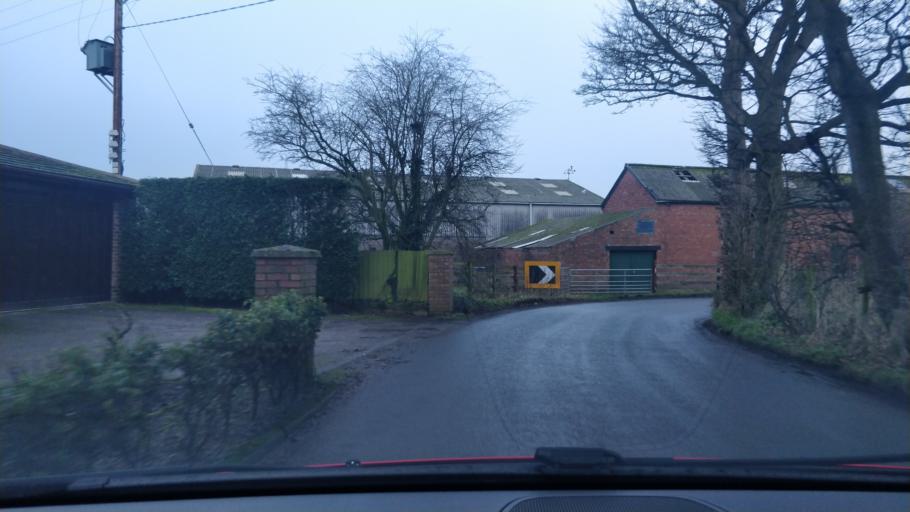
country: GB
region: England
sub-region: Lancashire
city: Banks
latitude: 53.6673
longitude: -2.8751
